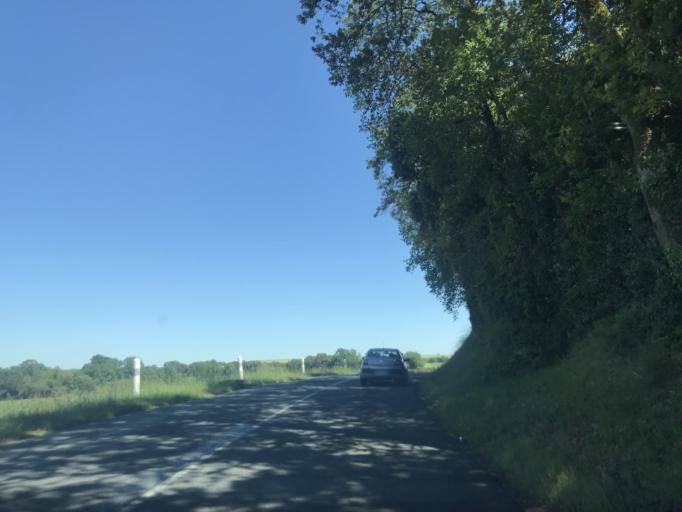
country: FR
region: Poitou-Charentes
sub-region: Departement de la Charente-Maritime
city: Meschers-sur-Gironde
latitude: 45.5930
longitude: -0.9689
